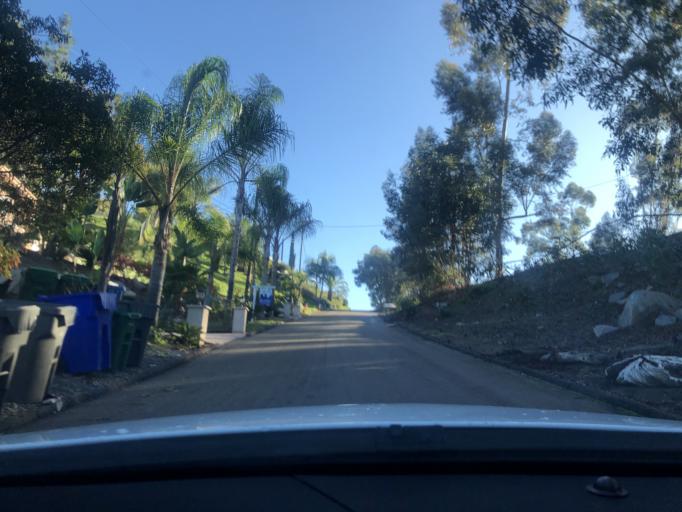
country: US
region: California
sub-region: San Diego County
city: Casa de Oro-Mount Helix
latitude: 32.7754
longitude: -116.9618
